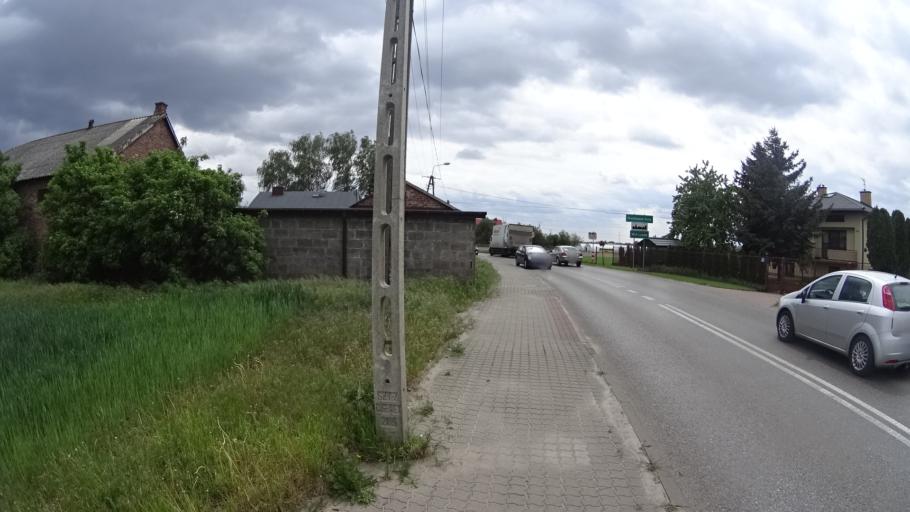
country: PL
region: Masovian Voivodeship
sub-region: Powiat warszawski zachodni
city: Babice
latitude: 52.2282
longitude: 20.8325
